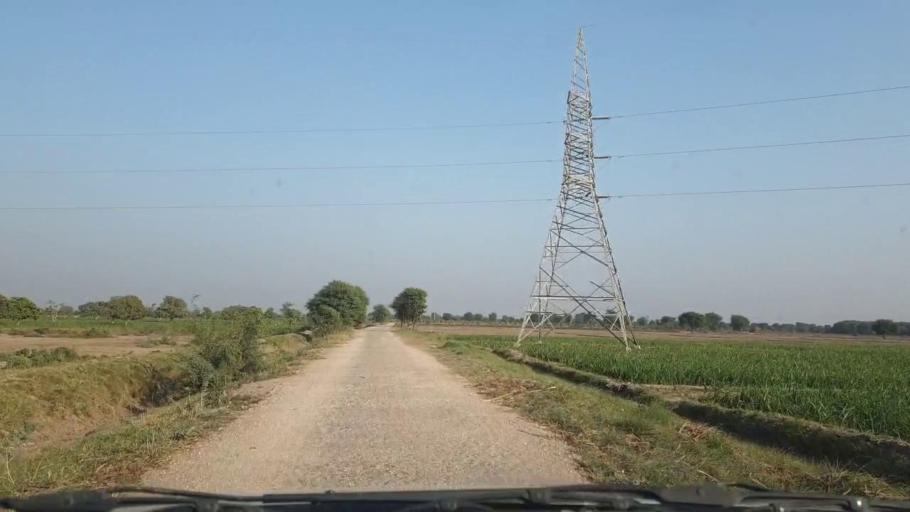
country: PK
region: Sindh
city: Chambar
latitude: 25.2160
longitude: 68.6827
